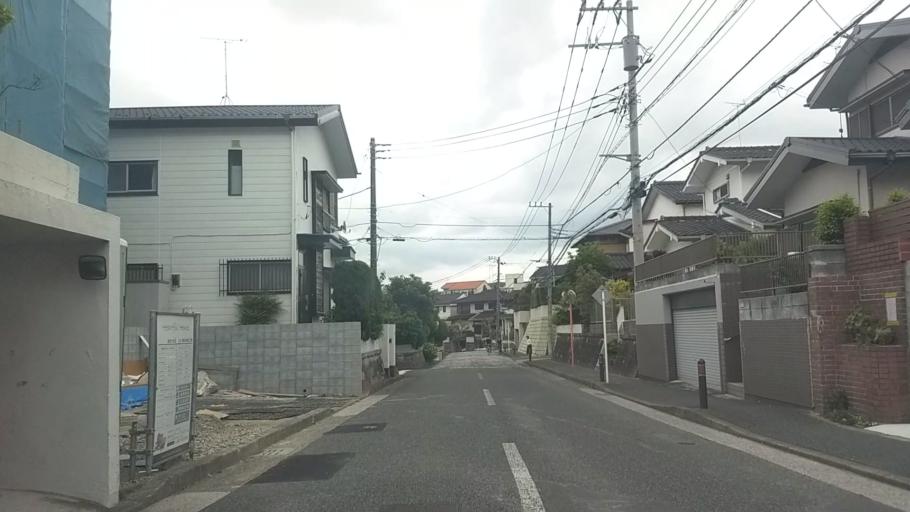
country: JP
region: Kanagawa
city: Fujisawa
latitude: 35.3553
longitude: 139.5070
